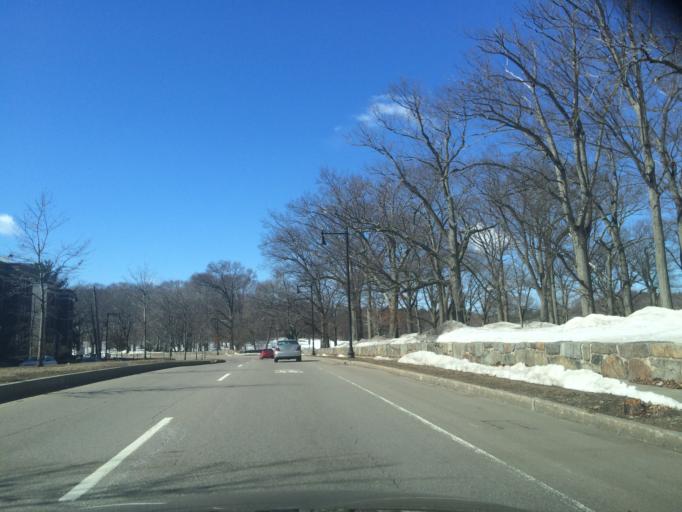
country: US
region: Massachusetts
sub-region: Suffolk County
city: Jamaica Plain
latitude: 42.2975
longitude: -71.0902
